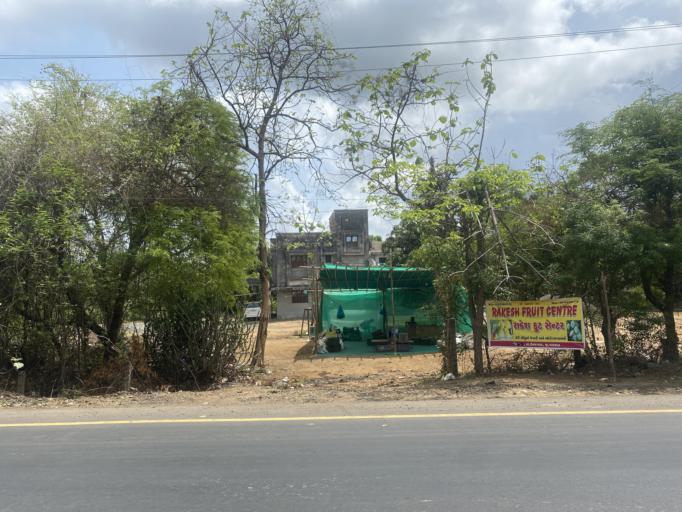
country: IN
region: Gujarat
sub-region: Valsad
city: Vapi
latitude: 20.3192
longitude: 72.8350
